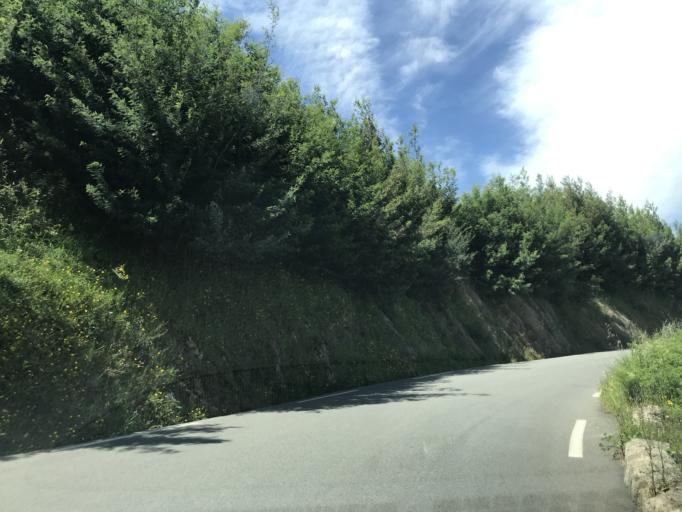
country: FR
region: Provence-Alpes-Cote d'Azur
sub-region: Departement du Var
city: Tanneron
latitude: 43.5887
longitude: 6.8786
